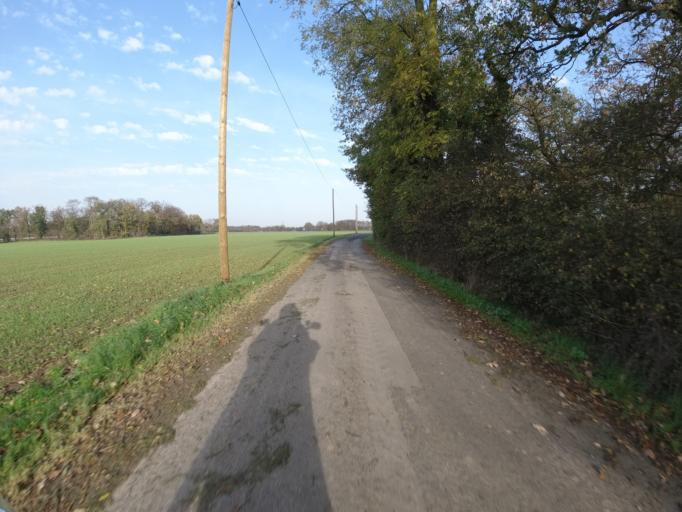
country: DE
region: North Rhine-Westphalia
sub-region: Regierungsbezirk Dusseldorf
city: Moers
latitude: 51.4273
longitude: 6.5656
